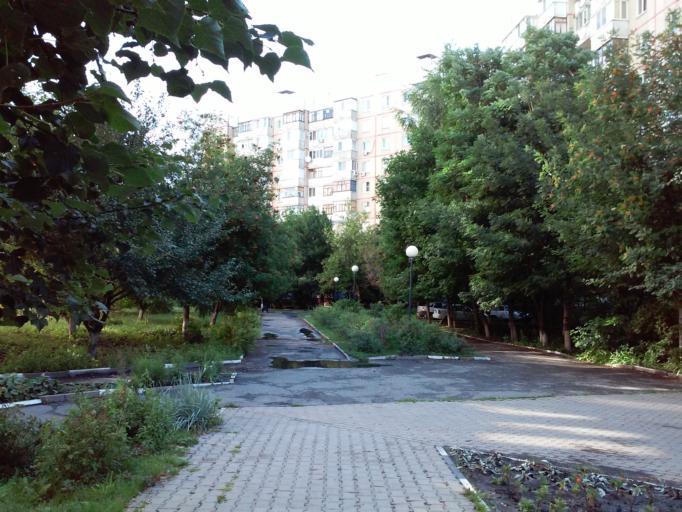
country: RU
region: Belgorod
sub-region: Belgorodskiy Rayon
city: Belgorod
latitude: 50.5589
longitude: 36.5689
